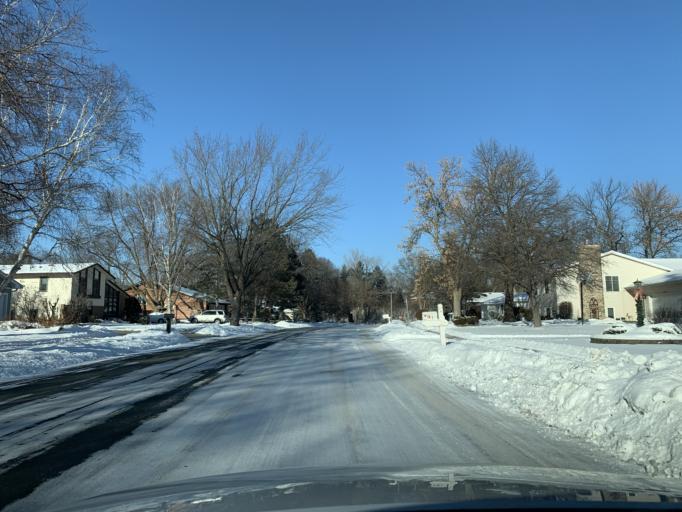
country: US
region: Minnesota
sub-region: Scott County
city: Savage
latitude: 44.8315
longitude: -93.3548
